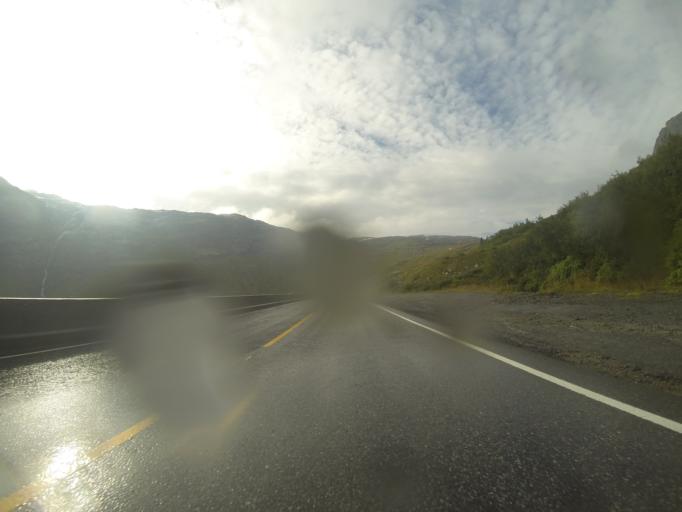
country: NO
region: Hordaland
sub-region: Odda
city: Odda
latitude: 59.8218
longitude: 6.7443
